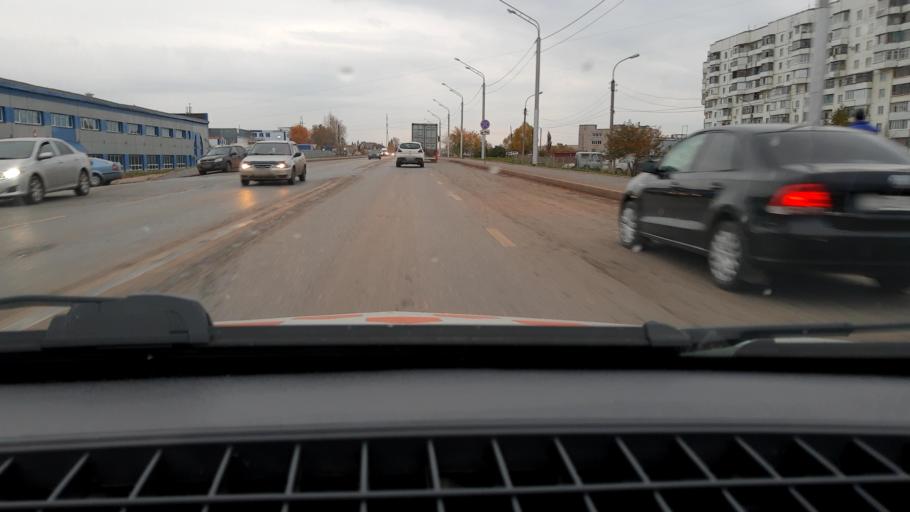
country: RU
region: Bashkortostan
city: Iglino
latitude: 54.7580
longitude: 56.2466
